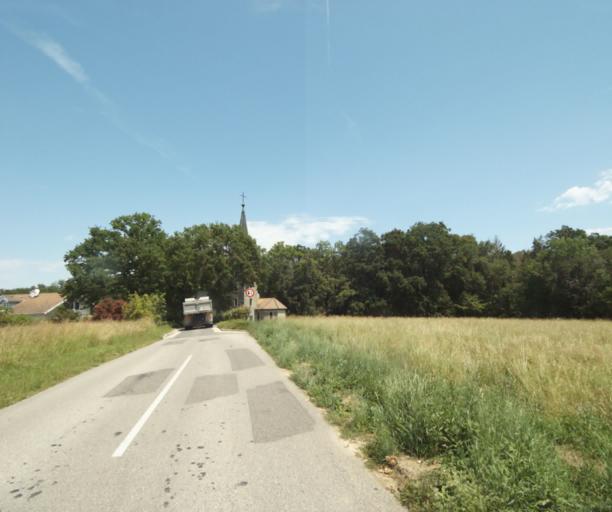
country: FR
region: Rhone-Alpes
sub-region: Departement de la Haute-Savoie
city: Messery
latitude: 46.3602
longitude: 6.3054
